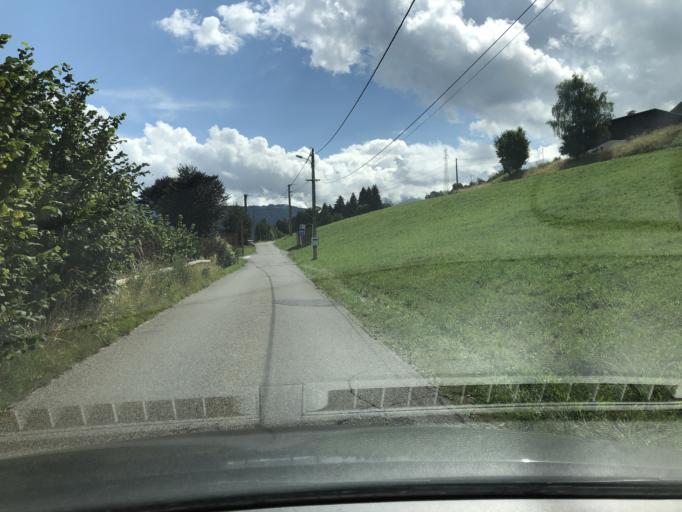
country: FR
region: Rhone-Alpes
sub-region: Departement de la Haute-Savoie
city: Domancy
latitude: 45.8960
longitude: 6.6558
